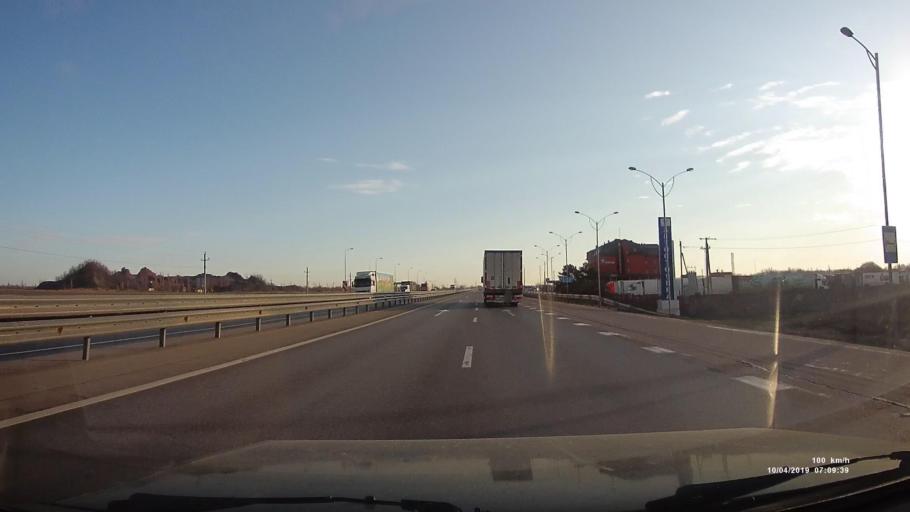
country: RU
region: Rostov
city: Mayskiy
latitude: 47.6892
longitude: 40.0797
